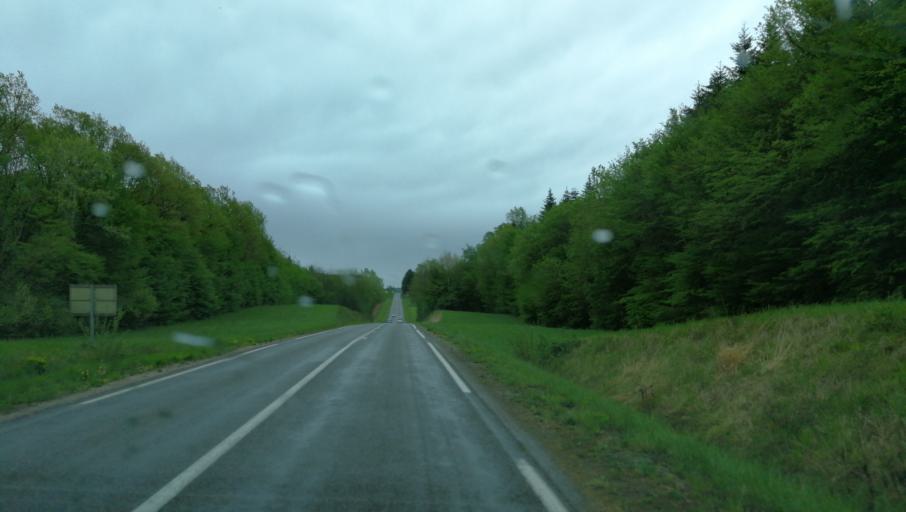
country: FR
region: Franche-Comte
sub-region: Departement du Jura
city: Montmorot
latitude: 46.6984
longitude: 5.4890
